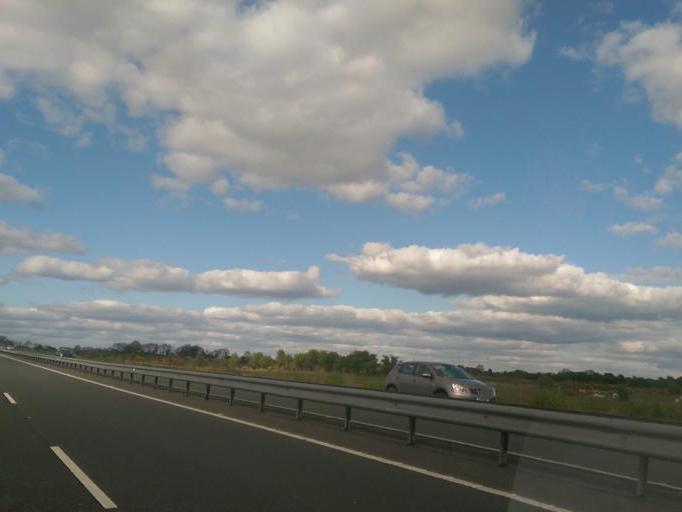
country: IE
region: Leinster
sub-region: An Iarmhi
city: Athlone
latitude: 53.3731
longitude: -8.0550
